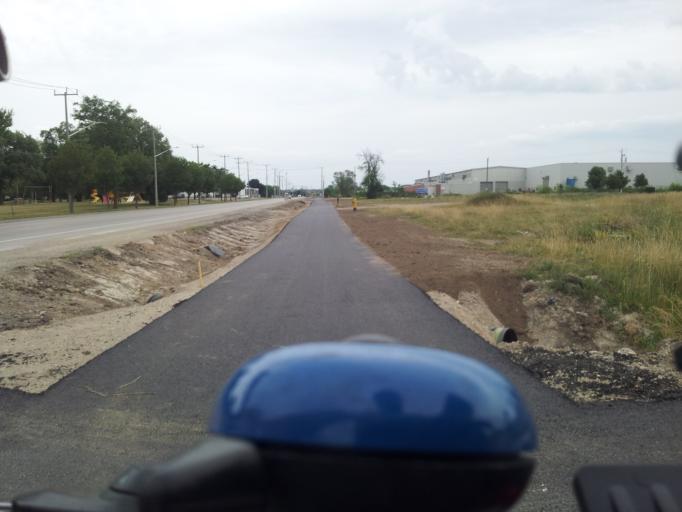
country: CA
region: Ontario
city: Stratford
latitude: 43.3593
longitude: -81.0041
